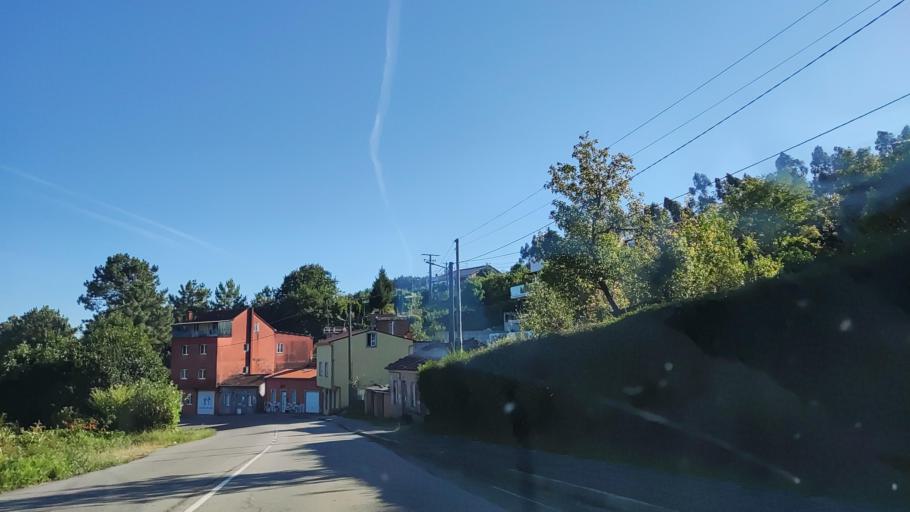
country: ES
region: Galicia
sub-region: Provincia da Coruna
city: Boiro
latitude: 42.6548
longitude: -8.8805
